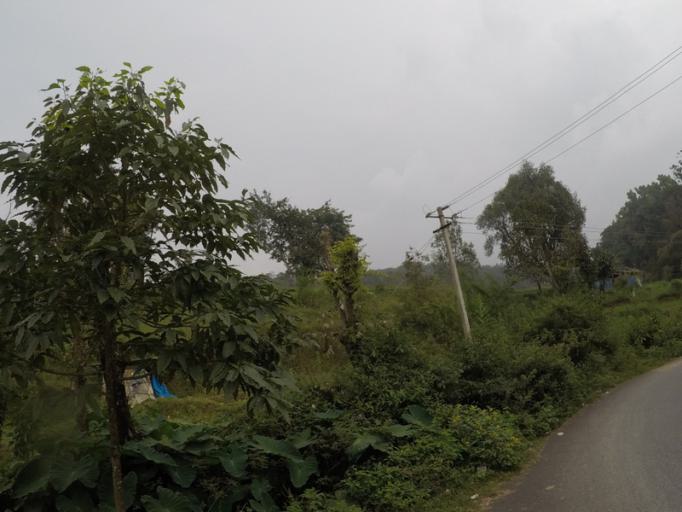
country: IN
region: Karnataka
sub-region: Chikmagalur
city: Mudigere
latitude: 13.1693
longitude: 75.4818
